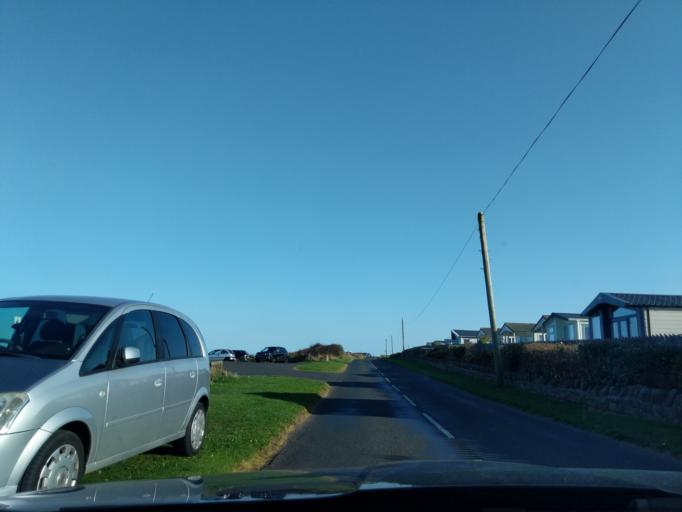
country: GB
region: England
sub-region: Northumberland
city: Lynemouth
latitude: 55.2307
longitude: -1.5323
